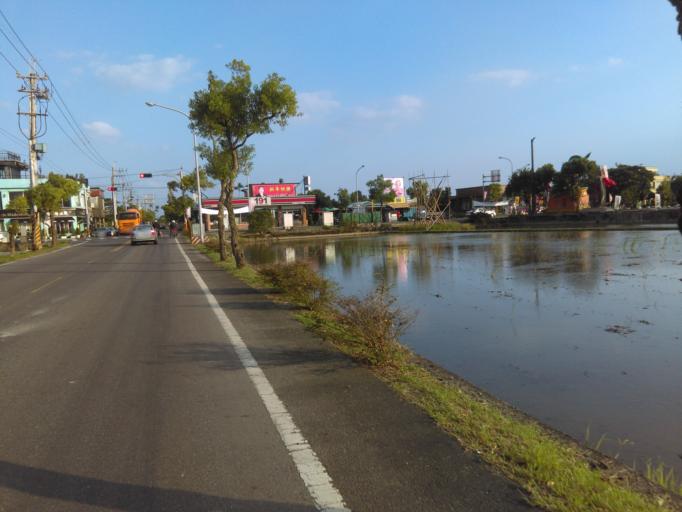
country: TW
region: Taiwan
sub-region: Yilan
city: Yilan
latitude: 24.7987
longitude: 121.7863
